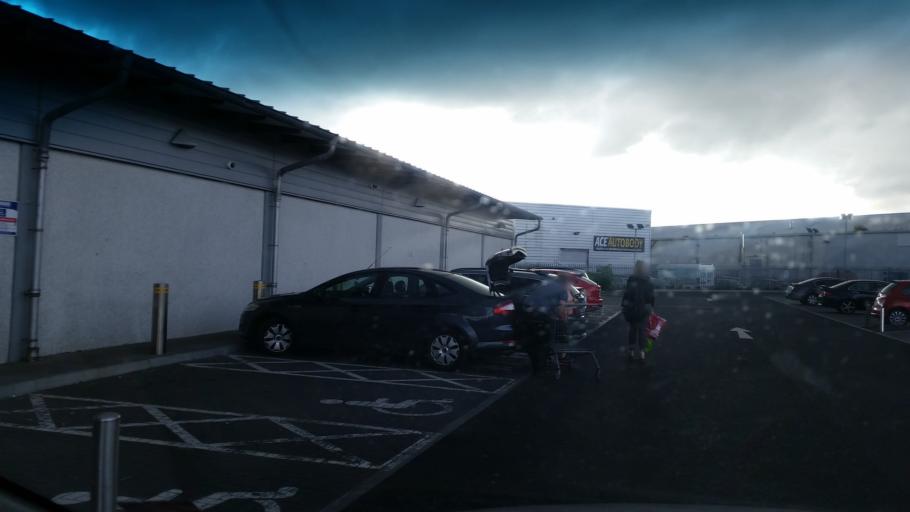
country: IE
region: Leinster
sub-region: Dublin City
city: Finglas
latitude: 53.3988
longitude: -6.3045
